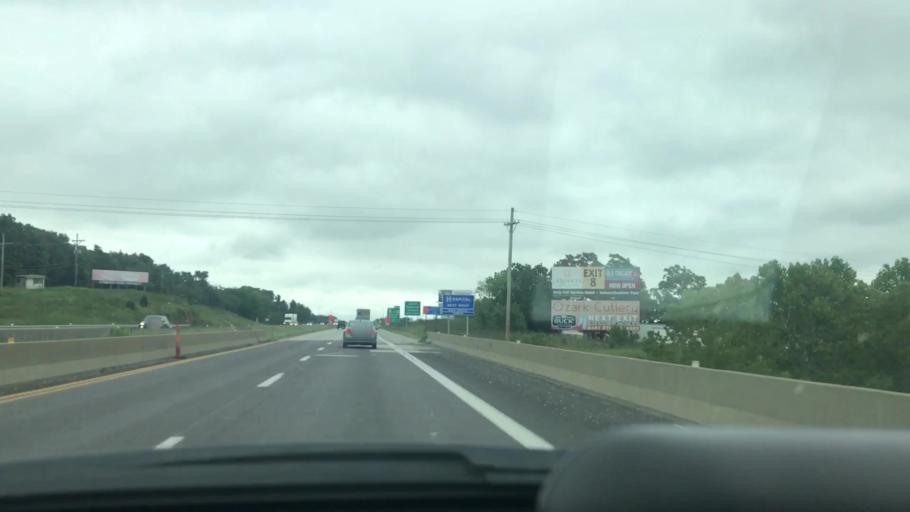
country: US
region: Missouri
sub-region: Jasper County
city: Joplin
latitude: 37.0310
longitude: -94.5227
